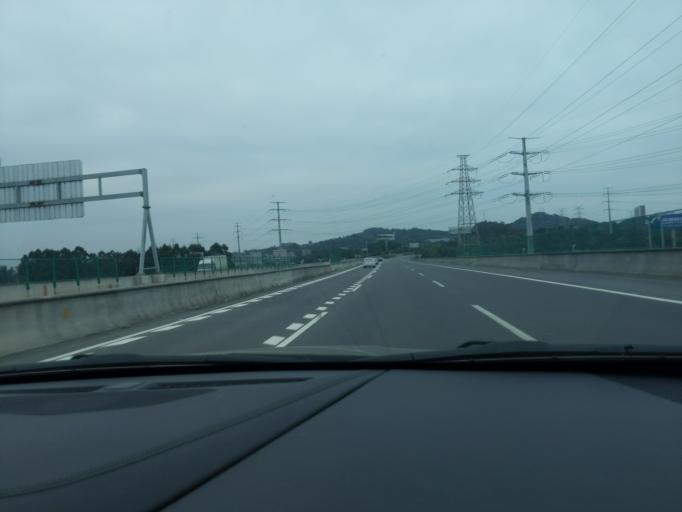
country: CN
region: Fujian
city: Shishi
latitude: 24.7496
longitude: 118.5869
